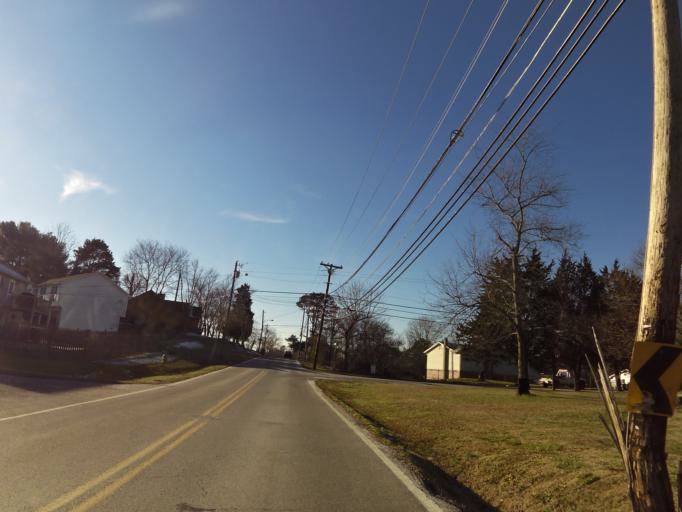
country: US
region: Tennessee
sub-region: Knox County
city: Knoxville
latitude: 35.9454
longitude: -84.0426
